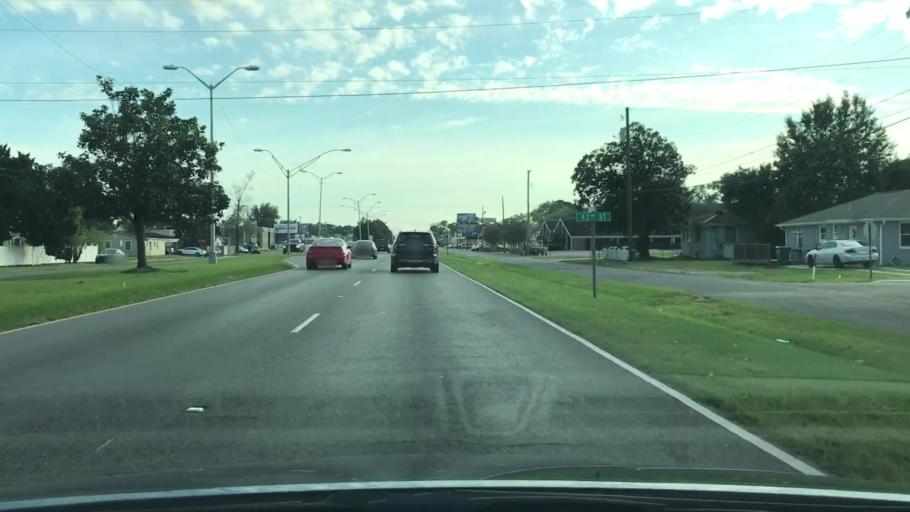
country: US
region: Louisiana
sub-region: Jefferson Parish
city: Metairie
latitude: 29.9886
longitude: -90.1559
